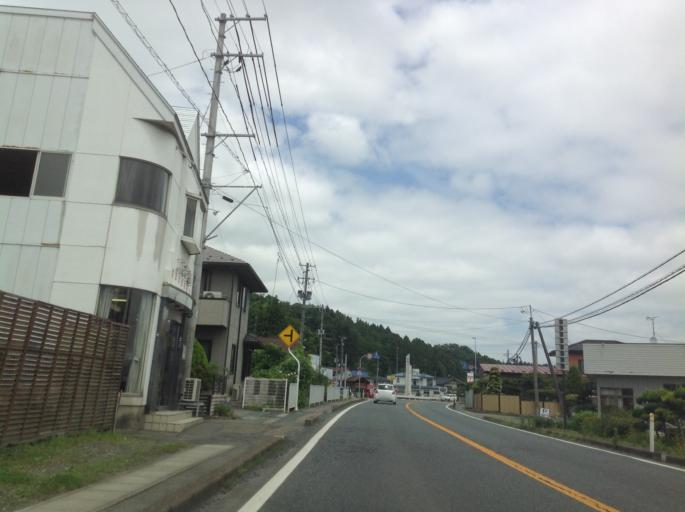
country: JP
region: Iwate
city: Mizusawa
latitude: 39.0960
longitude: 141.1340
